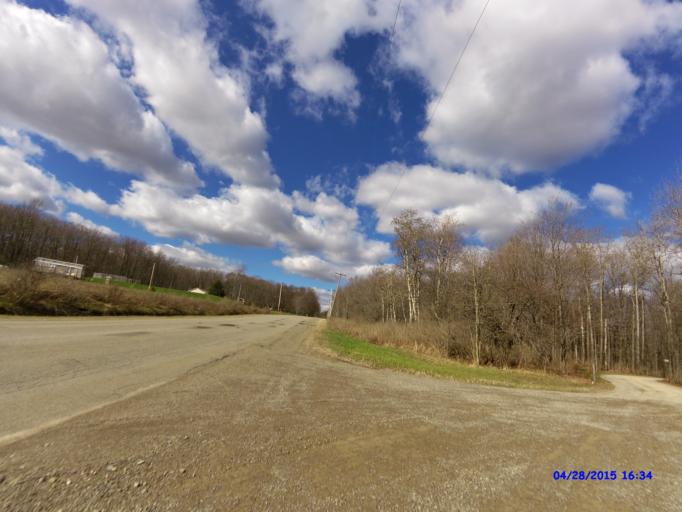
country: US
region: New York
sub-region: Cattaraugus County
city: Franklinville
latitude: 42.3908
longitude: -78.4362
